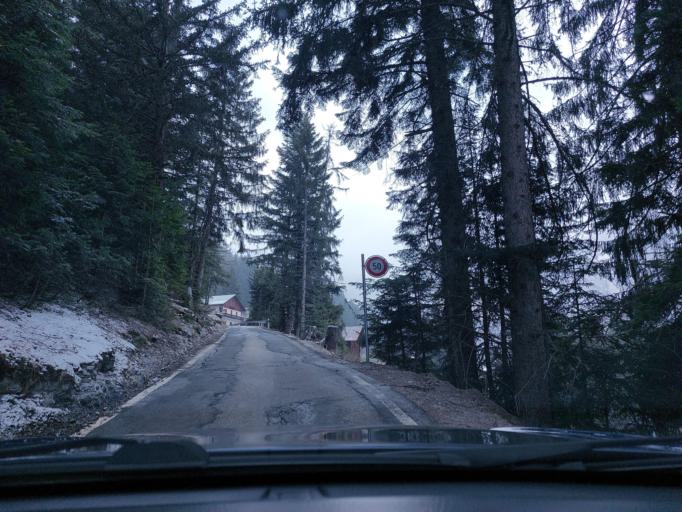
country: CH
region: Valais
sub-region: Sion District
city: Saviese
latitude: 46.2919
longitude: 7.3238
